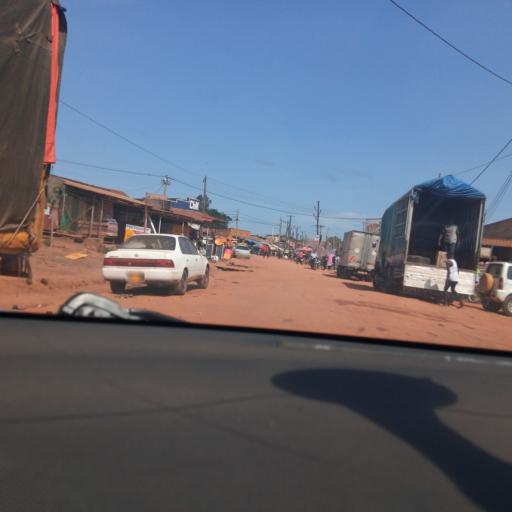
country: UG
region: Central Region
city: Masaka
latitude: -0.3167
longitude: 31.7593
